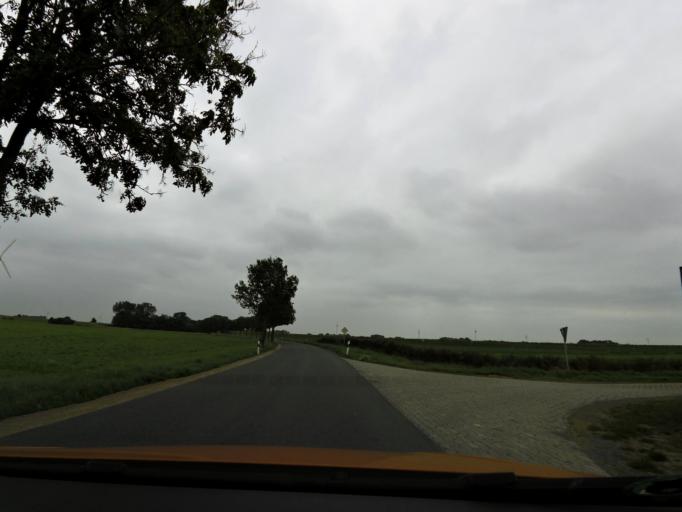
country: DE
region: Lower Saxony
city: Wirdum
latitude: 53.5040
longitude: 7.1582
